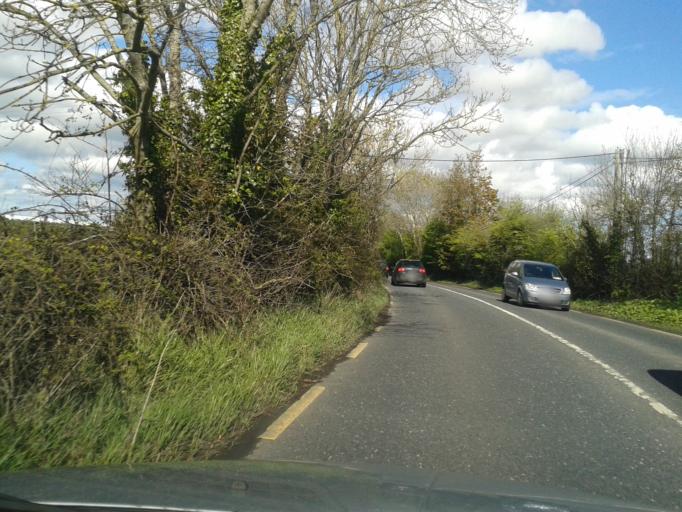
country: IE
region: Leinster
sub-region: Fingal County
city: Swords
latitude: 53.4782
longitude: -6.1975
